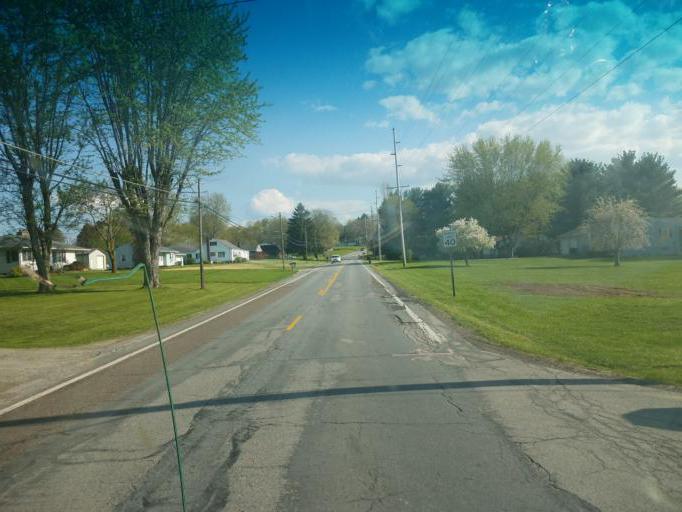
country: US
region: Ohio
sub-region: Wayne County
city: Shreve
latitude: 40.7189
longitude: -81.9440
